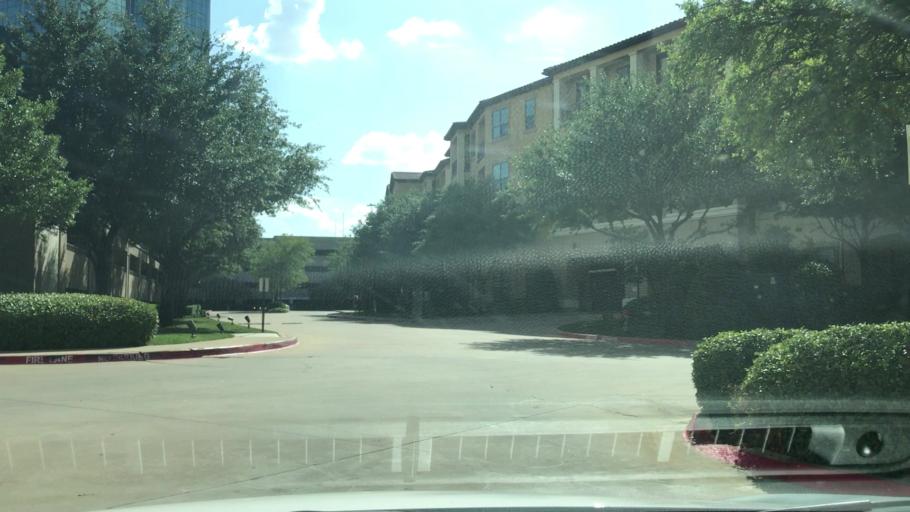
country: US
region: Texas
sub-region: Dallas County
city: Irving
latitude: 32.8726
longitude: -96.9417
